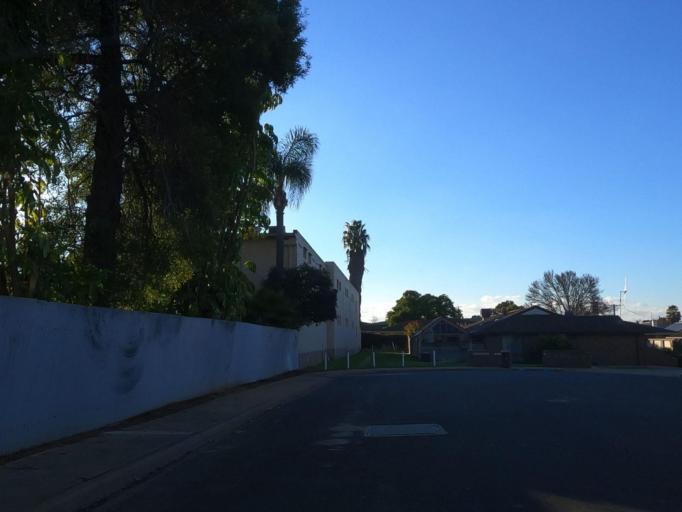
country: AU
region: Victoria
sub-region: Swan Hill
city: Swan Hill
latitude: -35.3466
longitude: 143.5629
